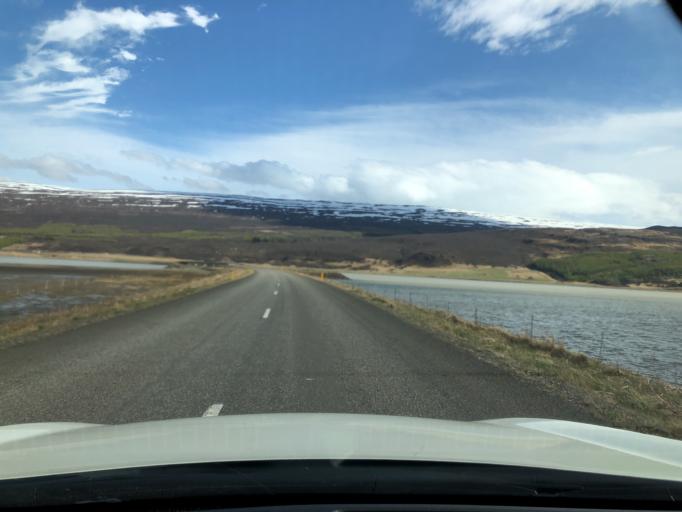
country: IS
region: East
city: Egilsstadir
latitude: 65.0729
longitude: -14.8642
